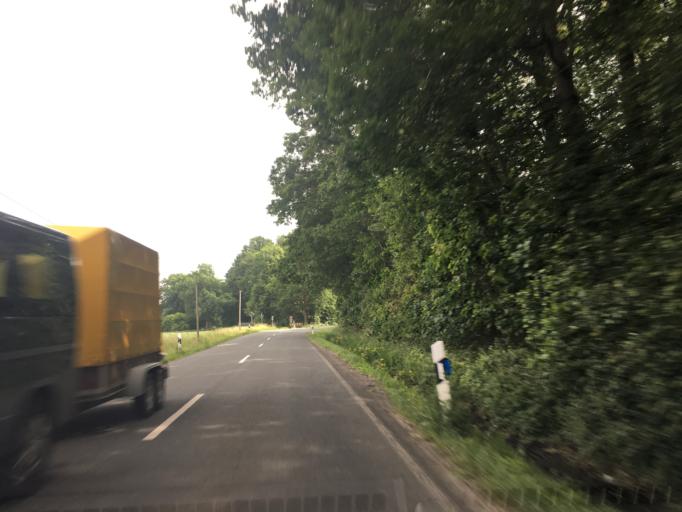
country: DE
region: North Rhine-Westphalia
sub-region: Regierungsbezirk Munster
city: Laer
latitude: 52.0969
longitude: 7.3468
